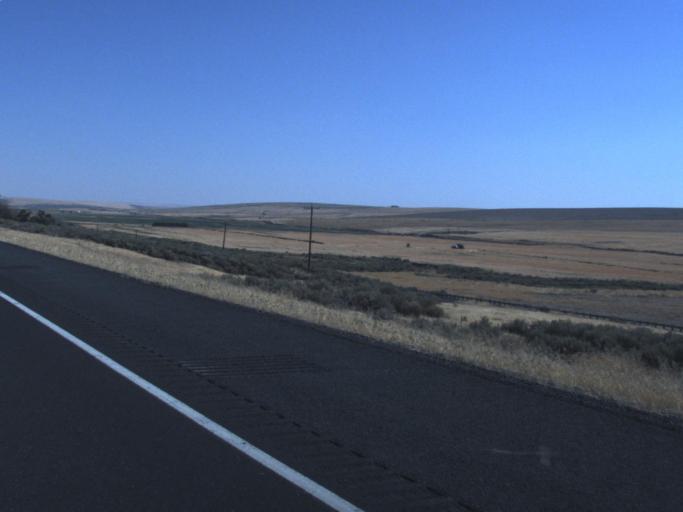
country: US
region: Washington
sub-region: Grant County
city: Warden
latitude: 47.0843
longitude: -118.9522
